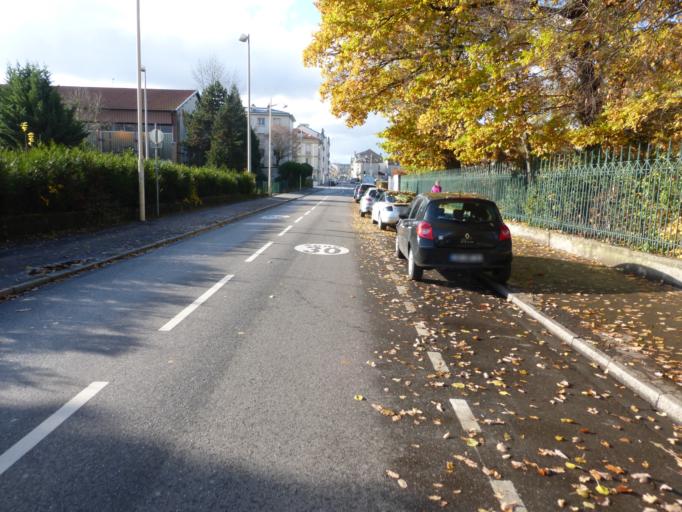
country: FR
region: Lorraine
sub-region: Departement de Meurthe-et-Moselle
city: Nancy
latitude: 48.6787
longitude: 6.1710
